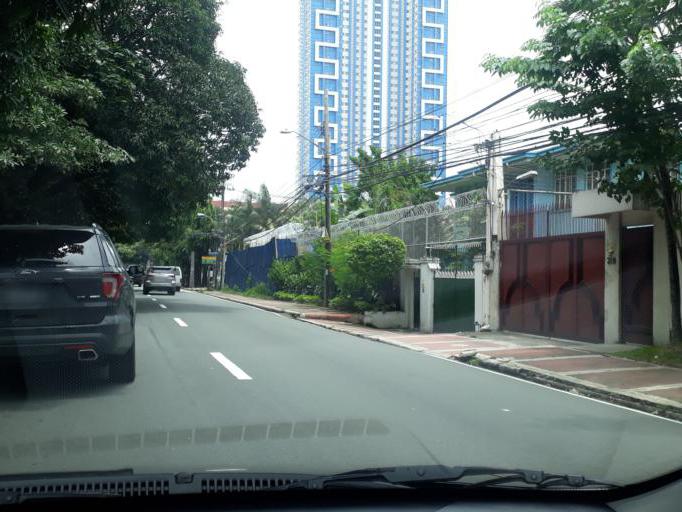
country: PH
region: Metro Manila
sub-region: San Juan
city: San Juan
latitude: 14.6158
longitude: 121.0335
